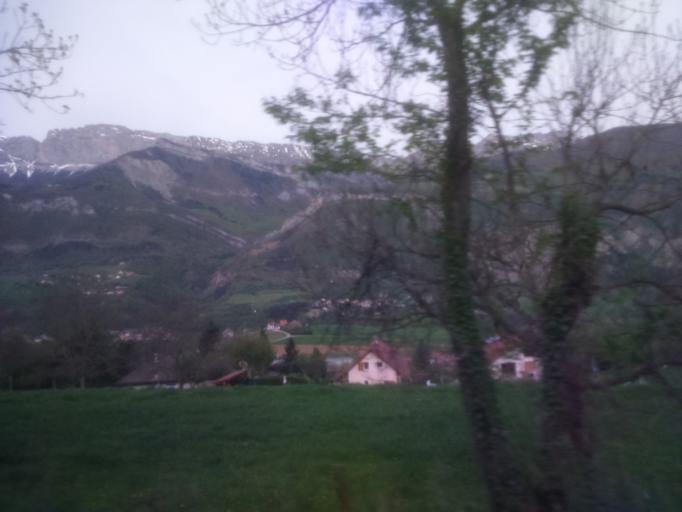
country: FR
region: Rhone-Alpes
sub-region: Departement de l'Isere
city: Vif
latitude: 45.0266
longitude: 5.6657
